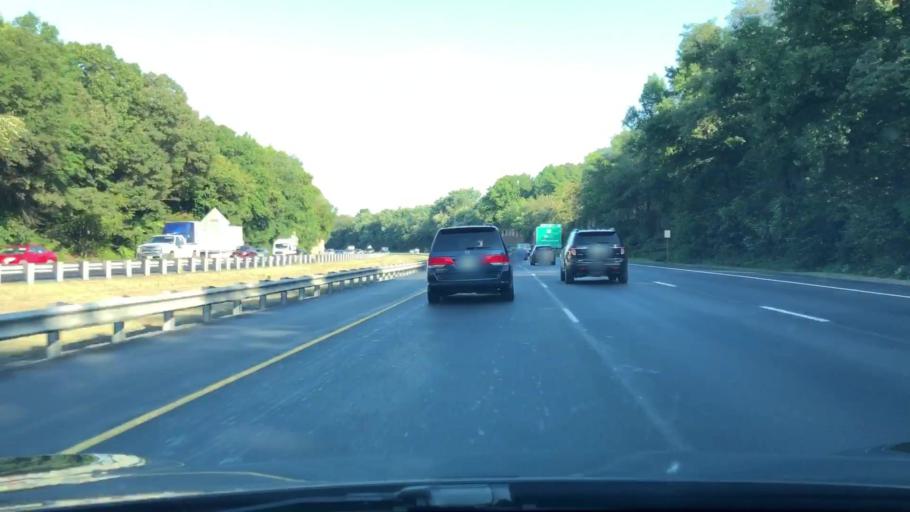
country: US
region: New Jersey
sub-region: Camden County
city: Haddon Heights
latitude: 39.8718
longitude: -75.0710
